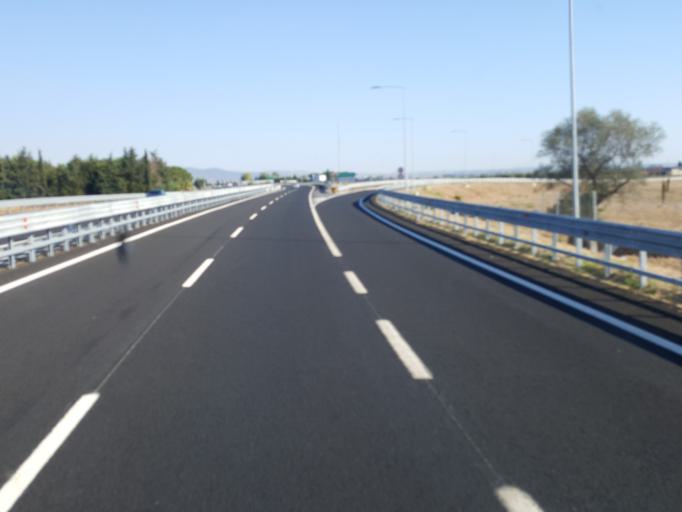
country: IT
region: Latium
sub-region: Provincia di Viterbo
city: Tarquinia
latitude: 42.2378
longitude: 11.7607
